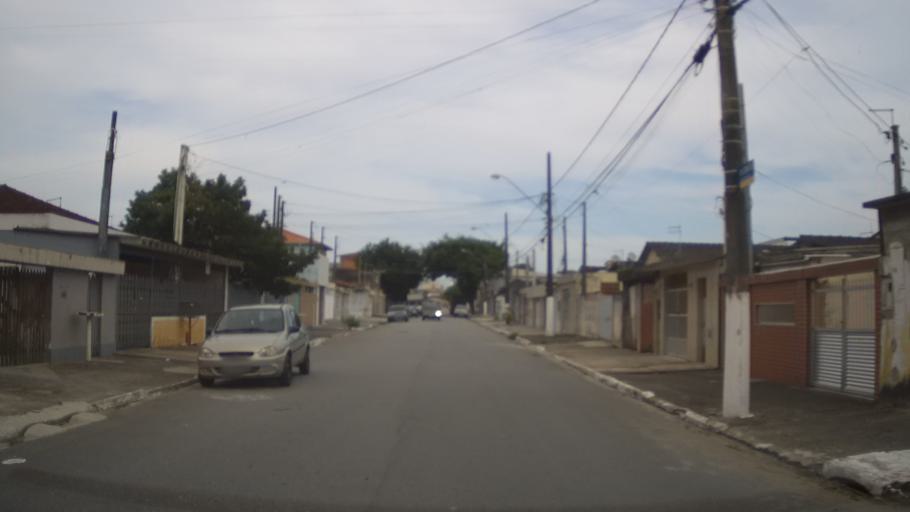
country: BR
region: Sao Paulo
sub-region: Praia Grande
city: Praia Grande
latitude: -24.0075
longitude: -46.4580
